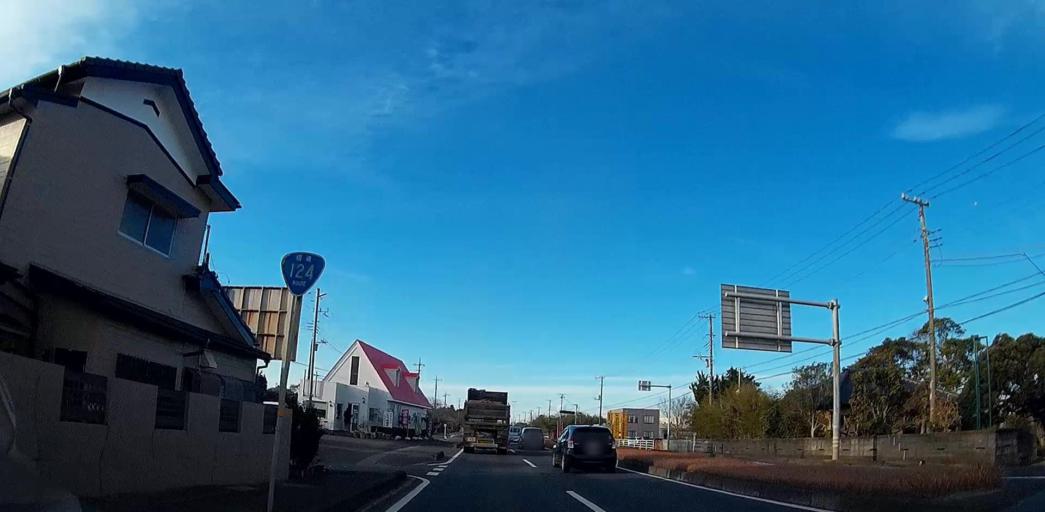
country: JP
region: Chiba
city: Omigawa
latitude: 35.8303
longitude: 140.7212
